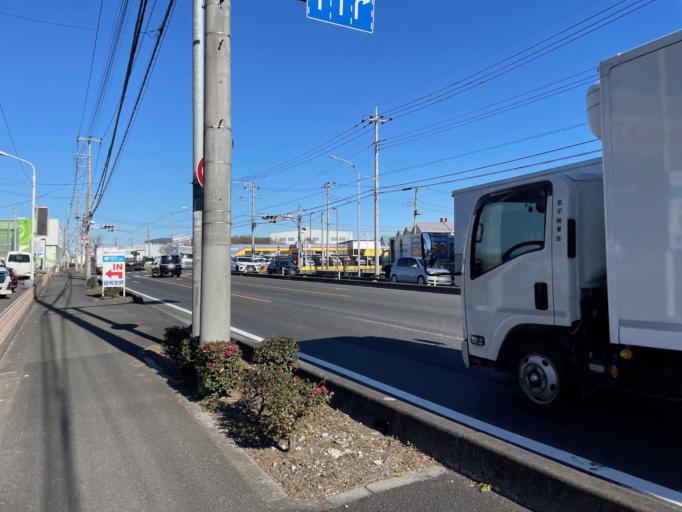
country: JP
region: Saitama
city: Ageoshimo
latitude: 35.9685
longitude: 139.6336
